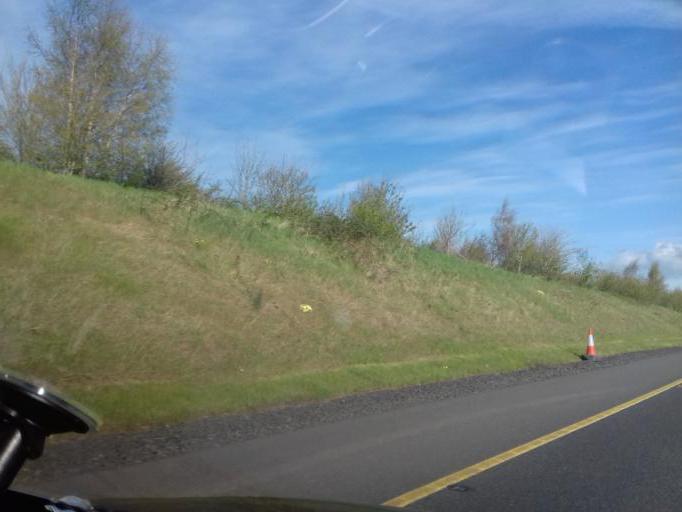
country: IE
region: Leinster
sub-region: An Mhi
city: Navan
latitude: 53.6608
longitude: -6.7578
